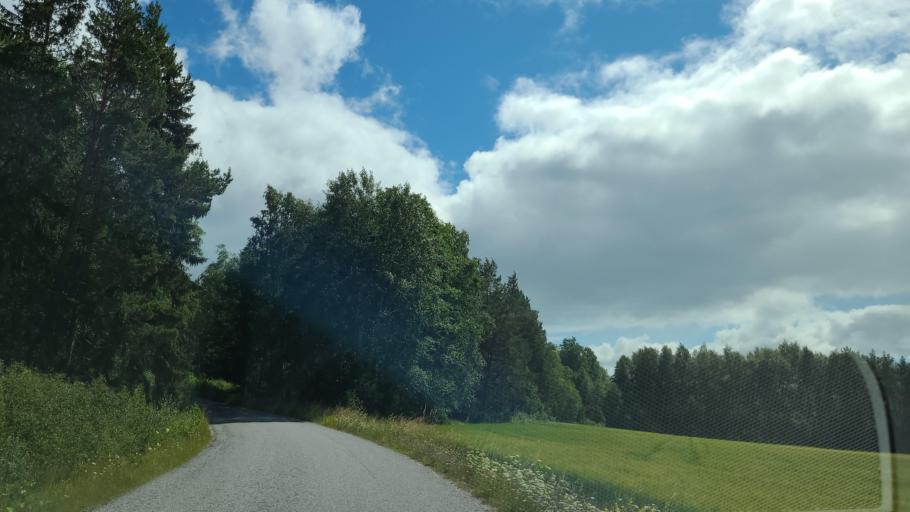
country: FI
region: Varsinais-Suomi
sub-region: Aboland-Turunmaa
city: Nagu
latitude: 60.1783
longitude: 22.0192
